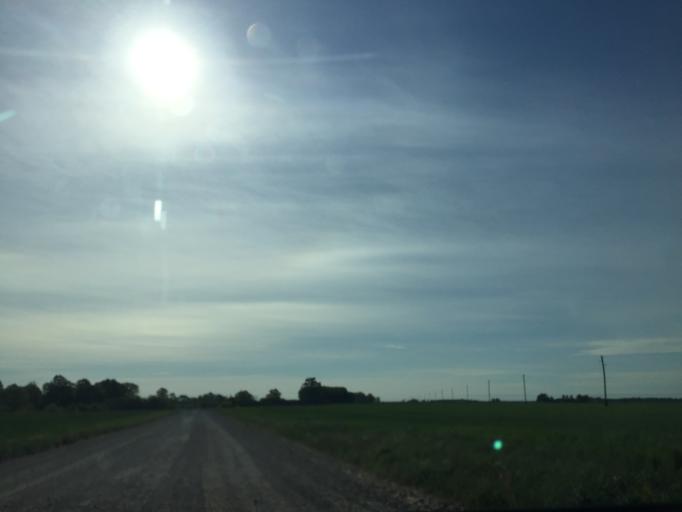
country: LV
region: Bauskas Rajons
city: Bauska
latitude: 56.2885
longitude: 24.3666
